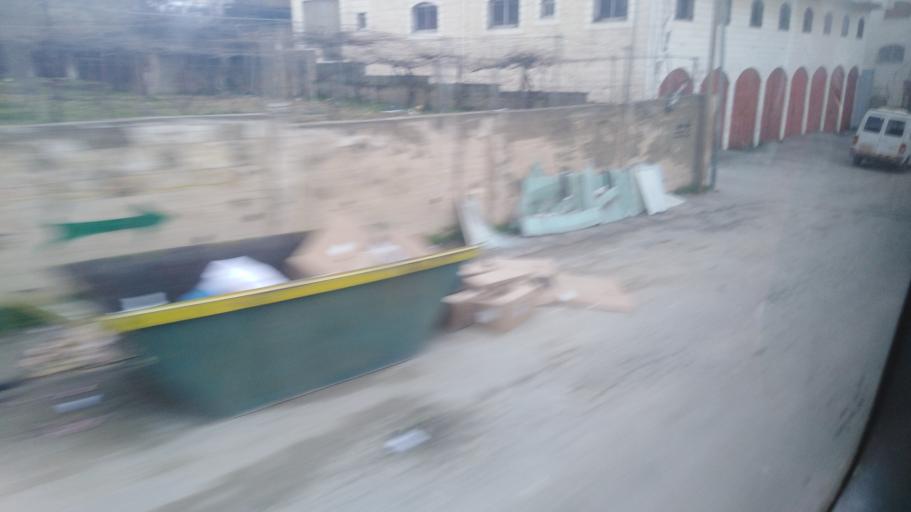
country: PS
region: West Bank
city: Hebron
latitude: 31.5249
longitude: 35.0763
